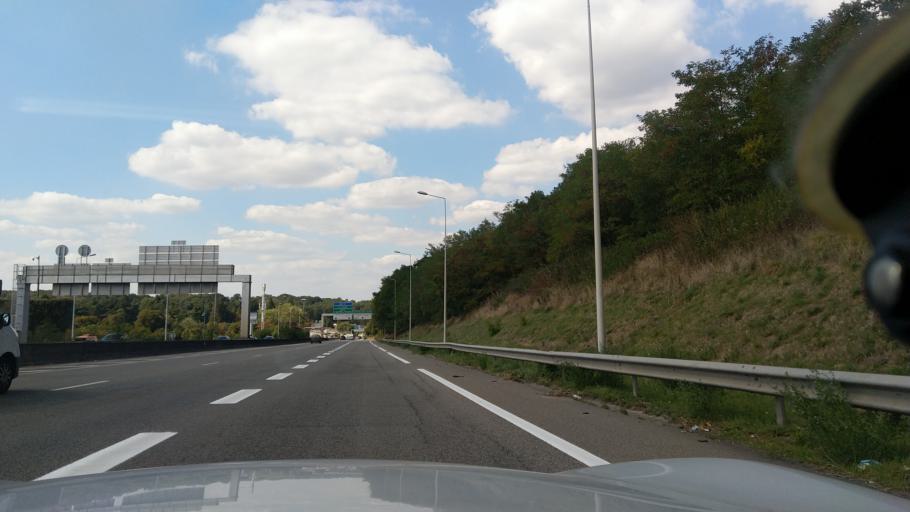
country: FR
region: Ile-de-France
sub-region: Departement des Yvelines
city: Viroflay
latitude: 48.7849
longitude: 2.1599
